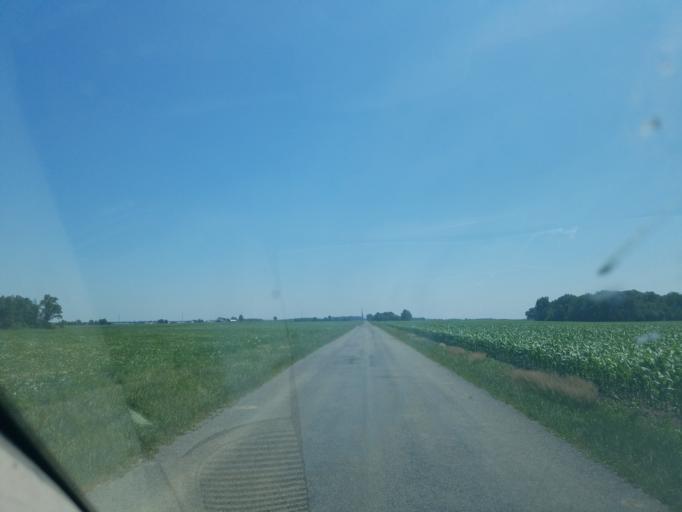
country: US
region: Ohio
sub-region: Mercer County
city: Rockford
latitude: 40.6694
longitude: -84.6988
